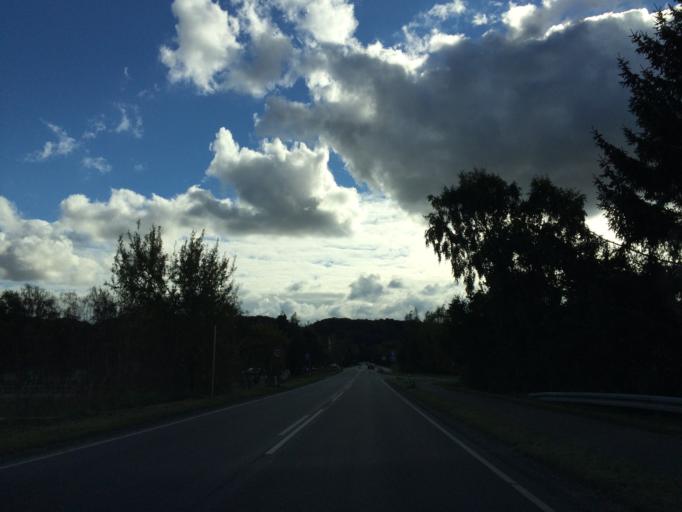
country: DK
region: Central Jutland
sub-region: Skanderborg Kommune
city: Ry
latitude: 56.1051
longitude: 9.7846
